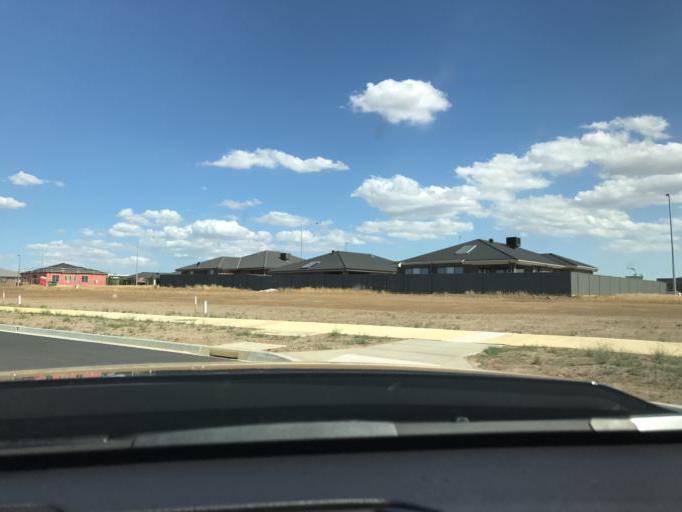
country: AU
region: Victoria
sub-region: Ballarat North
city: Newington
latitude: -37.5456
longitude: 143.7834
